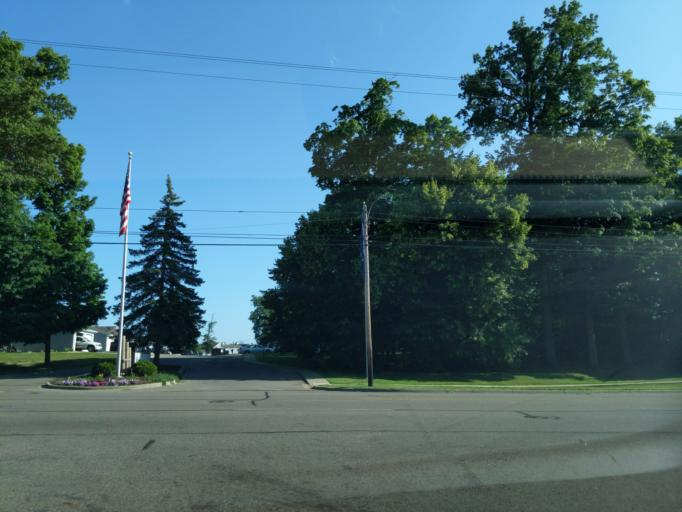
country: US
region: Michigan
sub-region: Eaton County
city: Waverly
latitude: 42.7339
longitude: -84.6183
